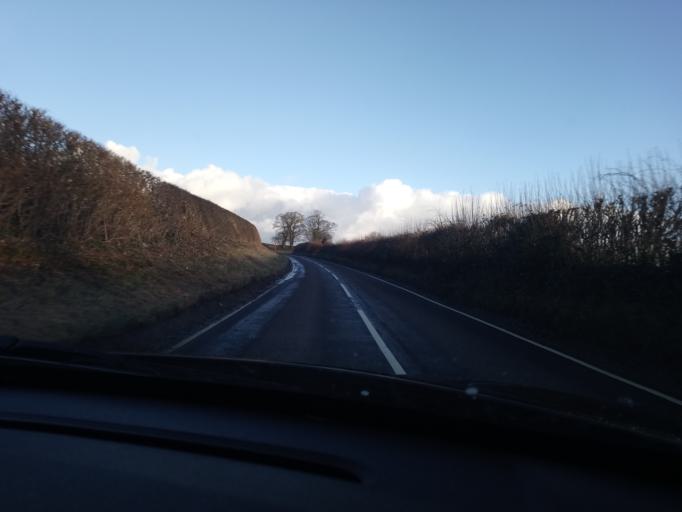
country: GB
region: England
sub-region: Shropshire
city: Wem
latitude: 52.8610
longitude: -2.7528
